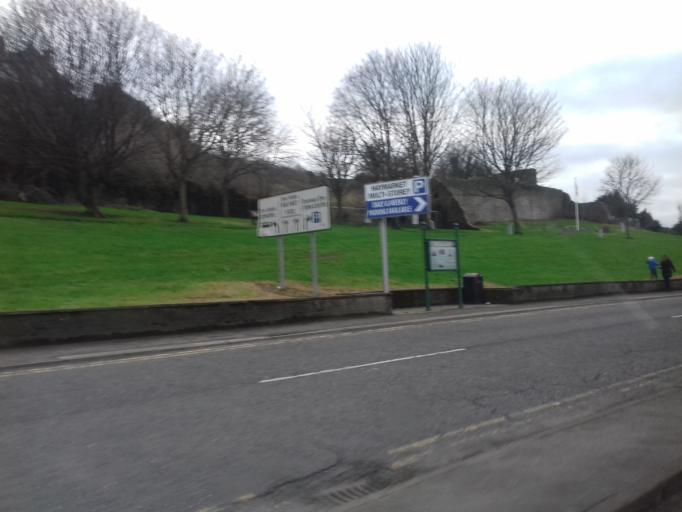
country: IE
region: Leinster
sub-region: Lu
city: Drogheda
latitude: 53.7126
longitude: -6.3506
